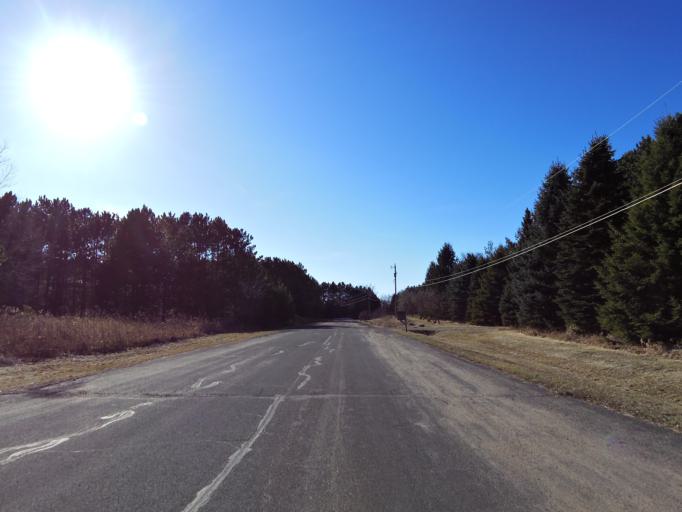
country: US
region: Minnesota
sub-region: Washington County
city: Oak Park Heights
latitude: 44.9862
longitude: -92.8237
